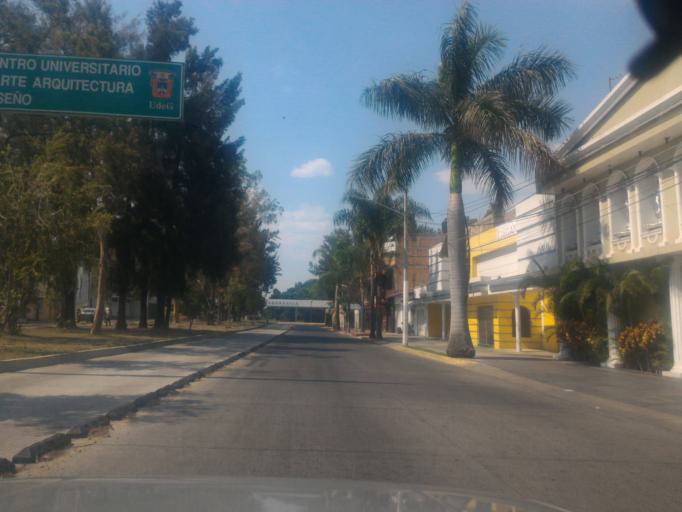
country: MX
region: Jalisco
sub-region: Zapopan
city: San Isidro
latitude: 20.7384
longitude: -103.3116
